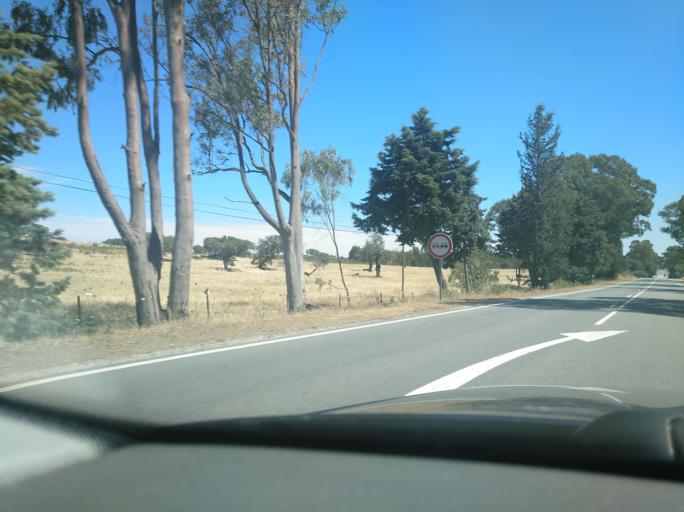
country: PT
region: Beja
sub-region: Almodovar
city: Almodovar
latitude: 37.5968
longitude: -8.0813
